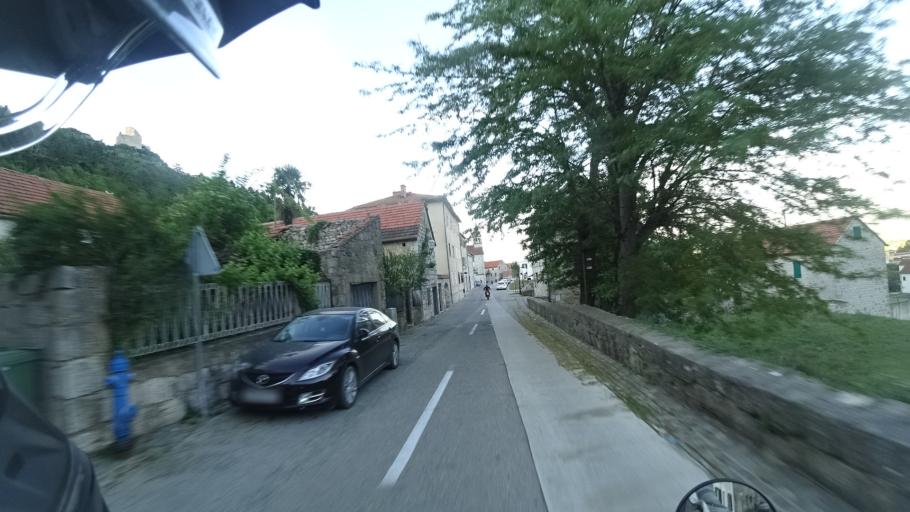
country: HR
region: Sibensko-Kniniska
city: Knin
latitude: 43.9100
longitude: 16.3942
